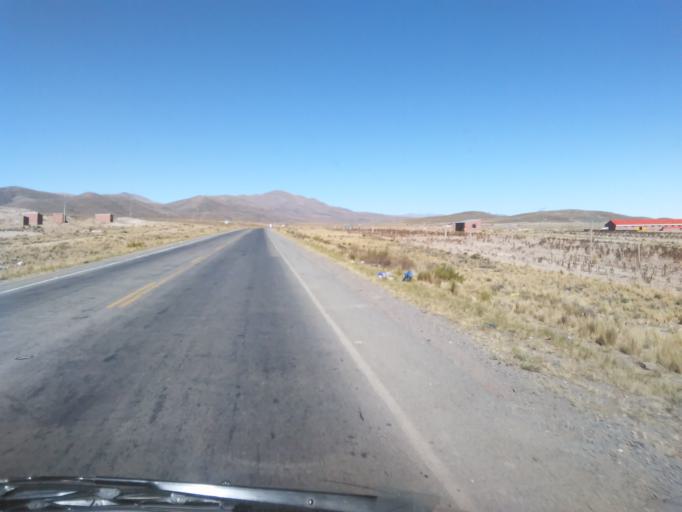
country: BO
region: Oruro
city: Oruro
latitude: -18.0280
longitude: -67.0230
